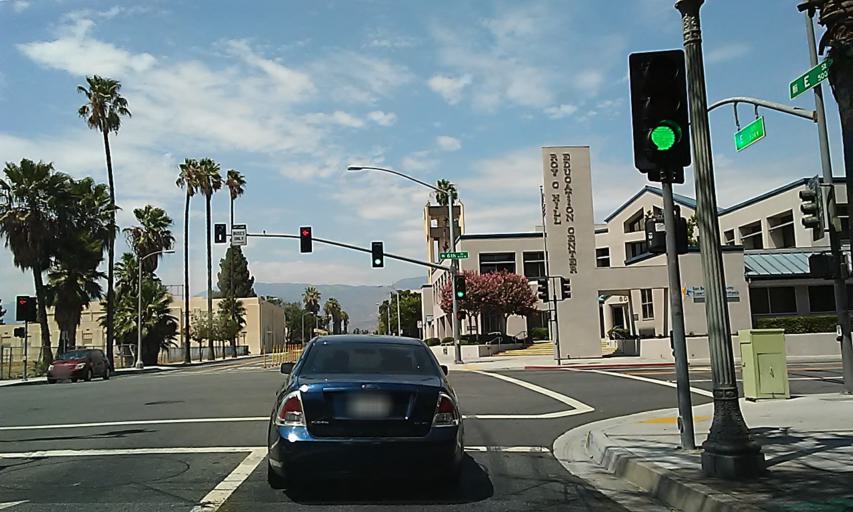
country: US
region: California
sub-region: San Bernardino County
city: San Bernardino
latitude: 34.1100
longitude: -117.2940
